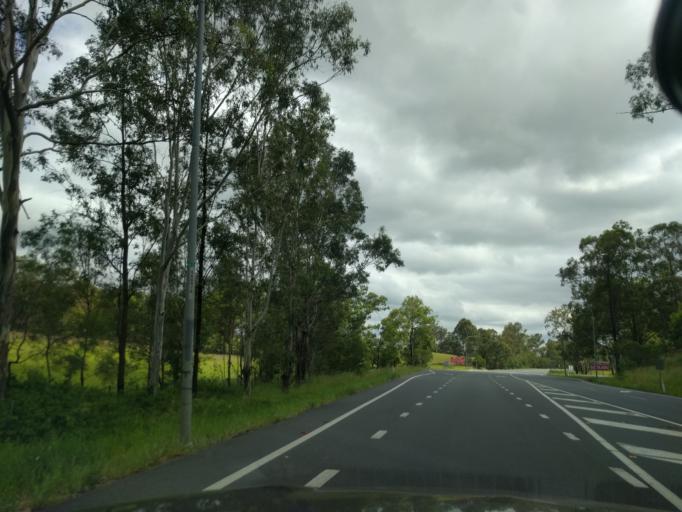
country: AU
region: Queensland
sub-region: Logan
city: Cedar Vale
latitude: -27.8655
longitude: 152.9996
